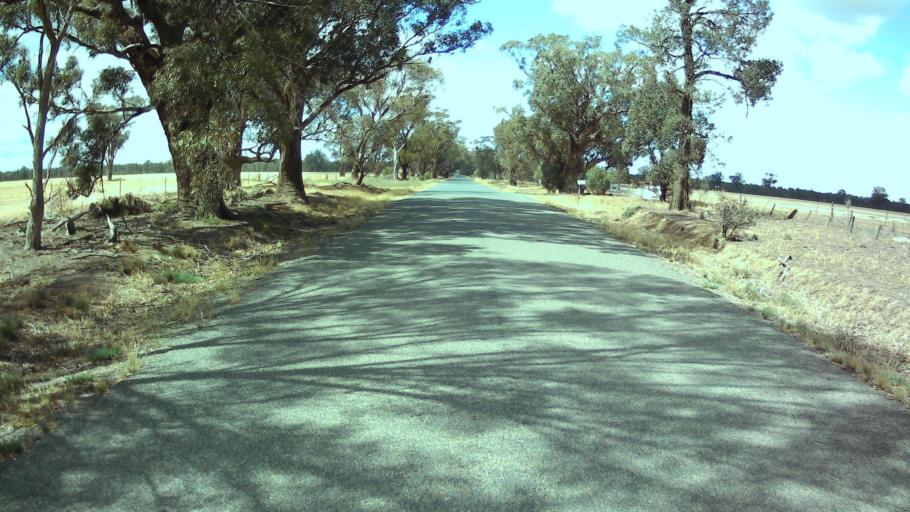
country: AU
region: New South Wales
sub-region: Weddin
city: Grenfell
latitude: -33.8917
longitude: 147.9224
